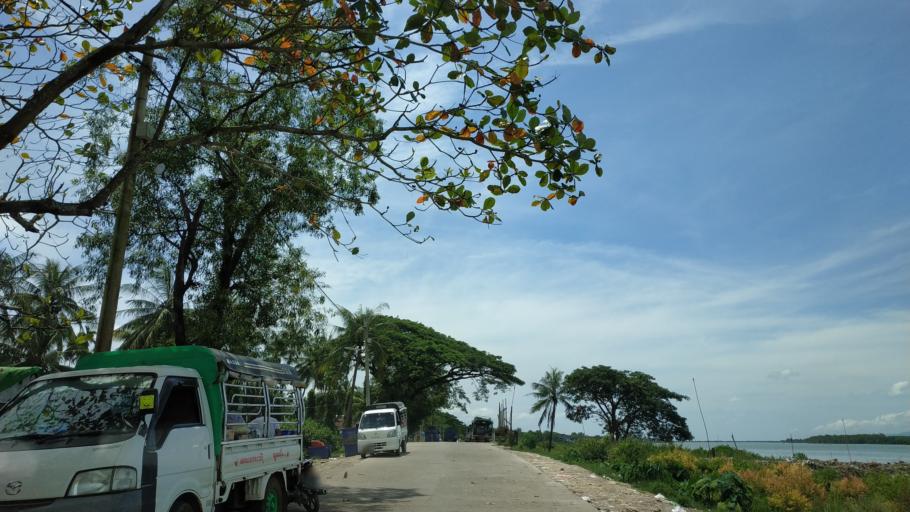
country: MM
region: Tanintharyi
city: Dawei
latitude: 14.0716
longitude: 98.1854
